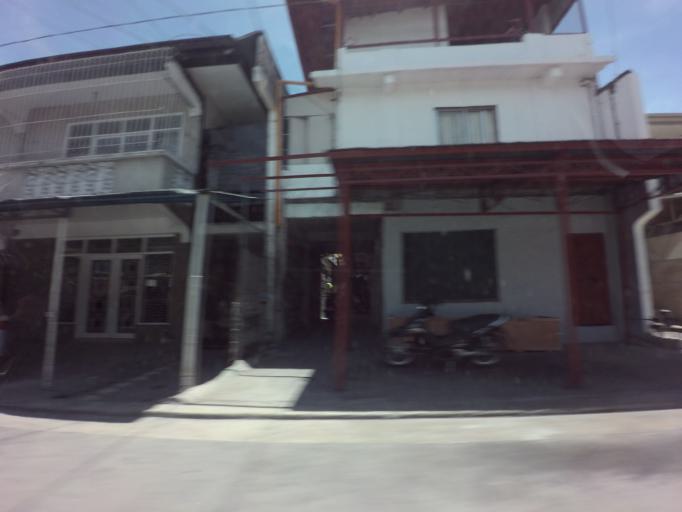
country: PH
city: Sambayanihan People's Village
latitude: 14.4901
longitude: 121.0343
